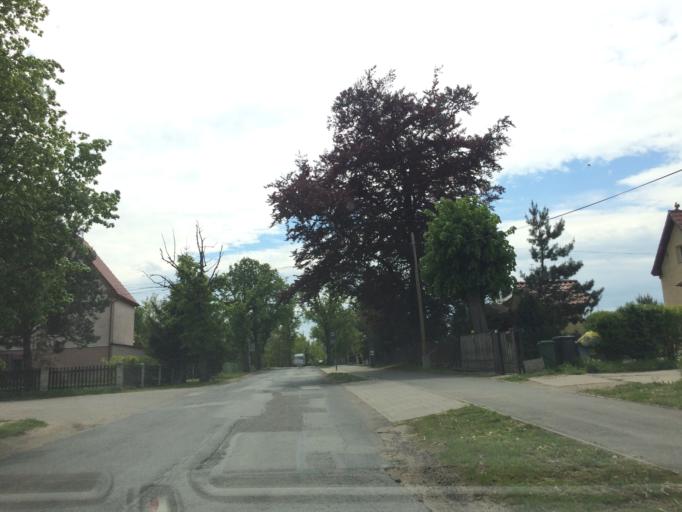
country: PL
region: Lower Silesian Voivodeship
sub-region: Powiat wroclawski
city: Smolec
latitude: 51.1636
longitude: 16.8785
